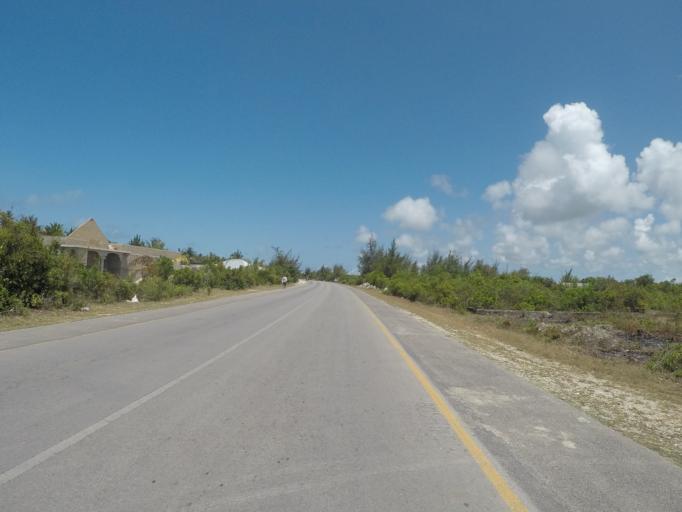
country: TZ
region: Zanzibar Central/South
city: Nganane
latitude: -6.3176
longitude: 39.5425
